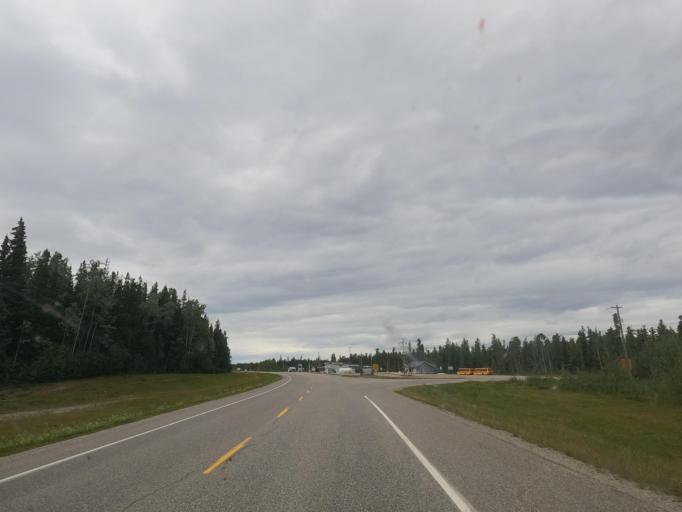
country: CA
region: Yukon
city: Watson Lake
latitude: 60.0481
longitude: -128.6506
